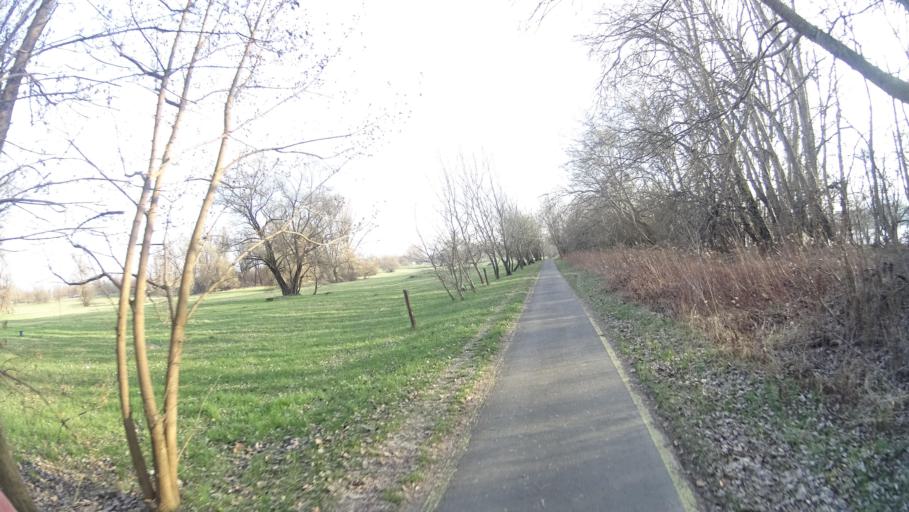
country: HU
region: Pest
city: Szodliget
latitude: 47.7417
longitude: 19.1360
